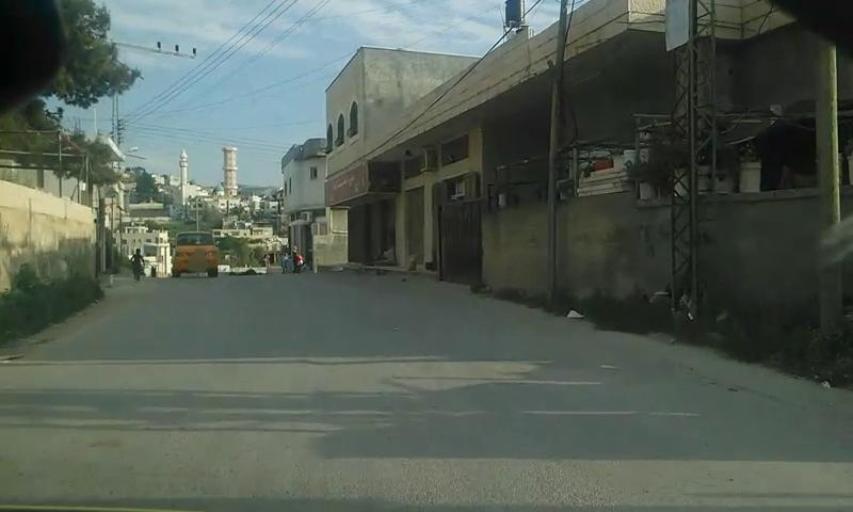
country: PS
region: West Bank
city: Nuba
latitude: 31.6098
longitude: 35.0345
